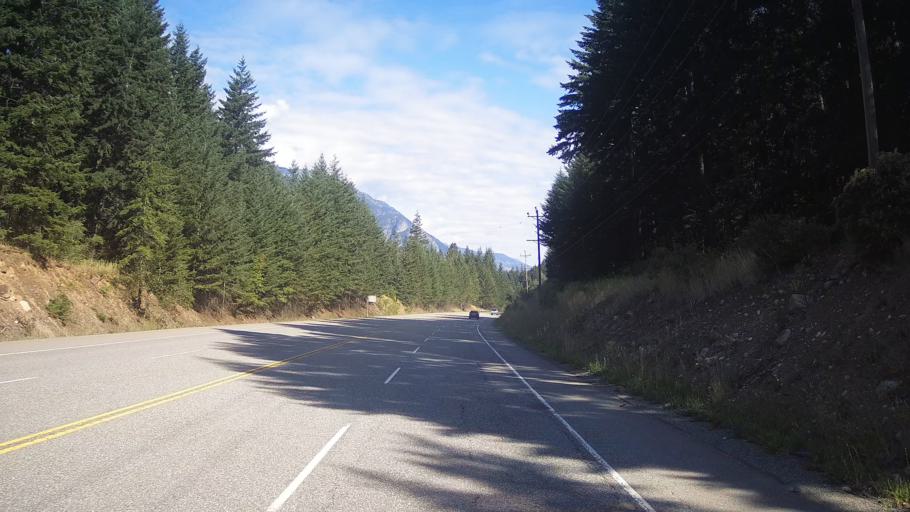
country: CA
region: British Columbia
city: Hope
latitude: 50.0486
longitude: -121.5402
